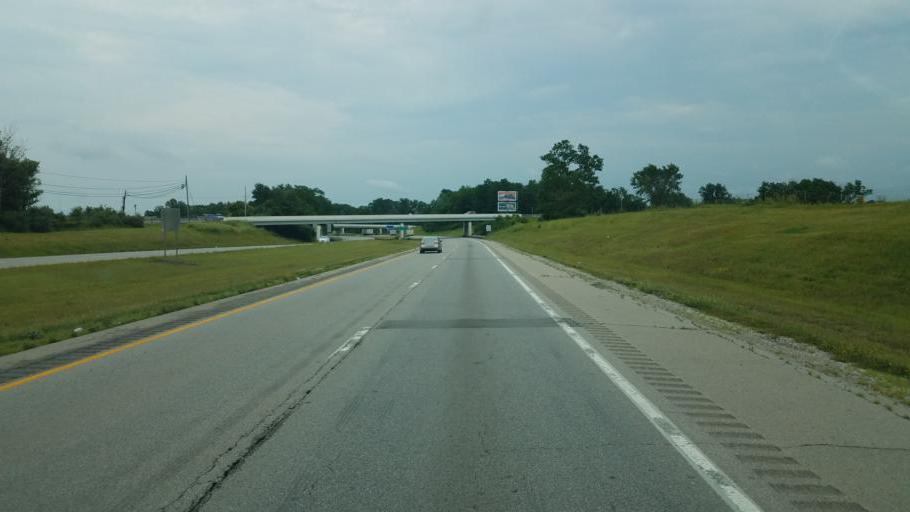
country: US
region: Ohio
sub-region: Richland County
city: Ontario
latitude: 40.7766
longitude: -82.5728
